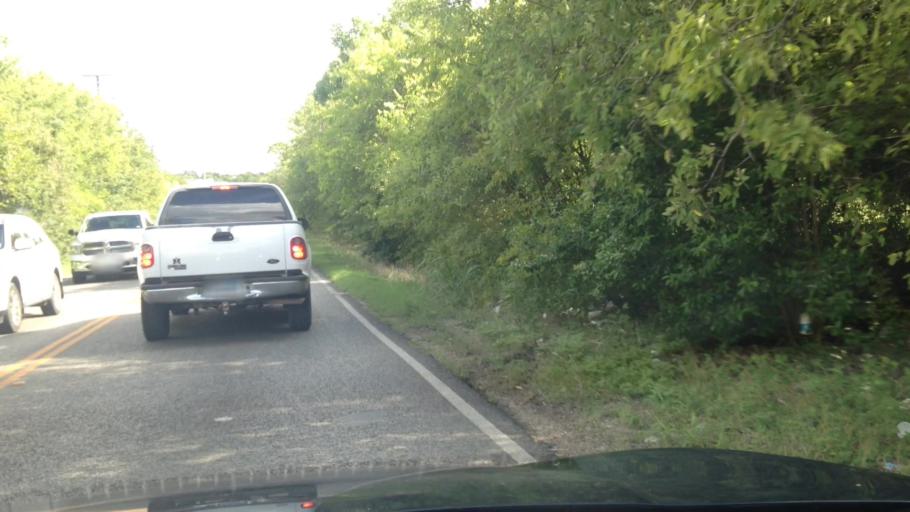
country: US
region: Texas
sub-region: Bexar County
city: Windcrest
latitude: 29.5772
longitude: -98.4008
